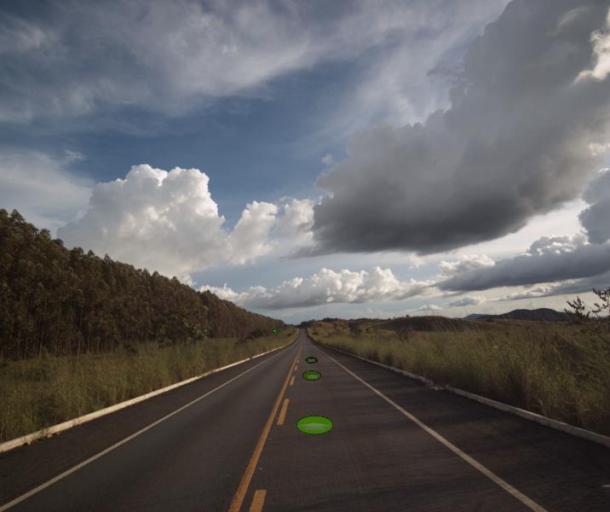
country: BR
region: Goias
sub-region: Niquelandia
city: Niquelandia
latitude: -14.6090
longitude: -48.5875
